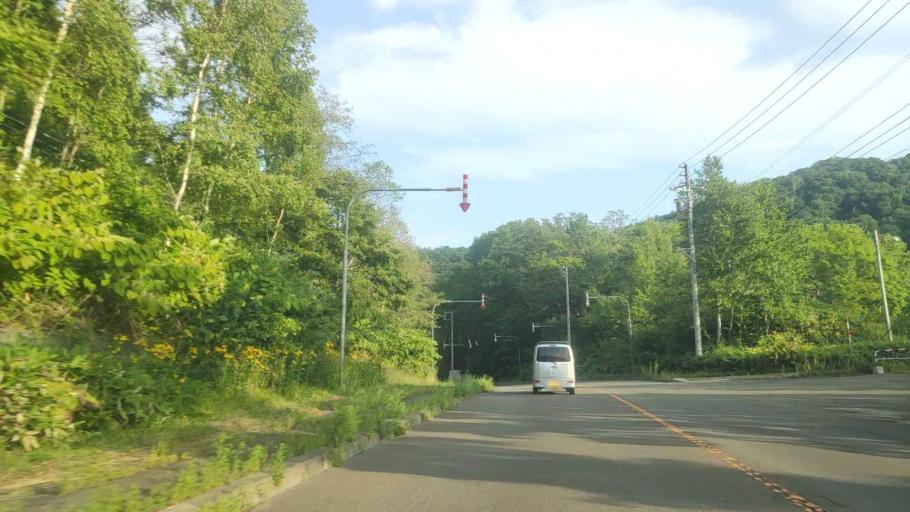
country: JP
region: Hokkaido
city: Iwamizawa
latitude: 43.0172
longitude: 141.9940
